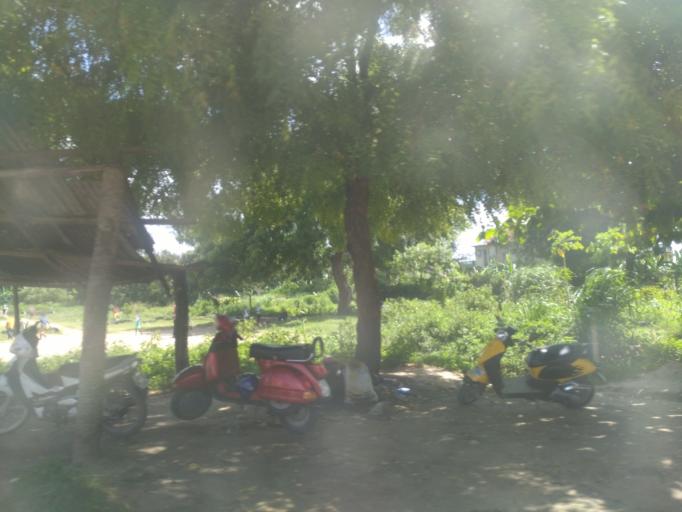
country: TZ
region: Zanzibar Urban/West
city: Zanzibar
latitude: -6.1697
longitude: 39.2071
